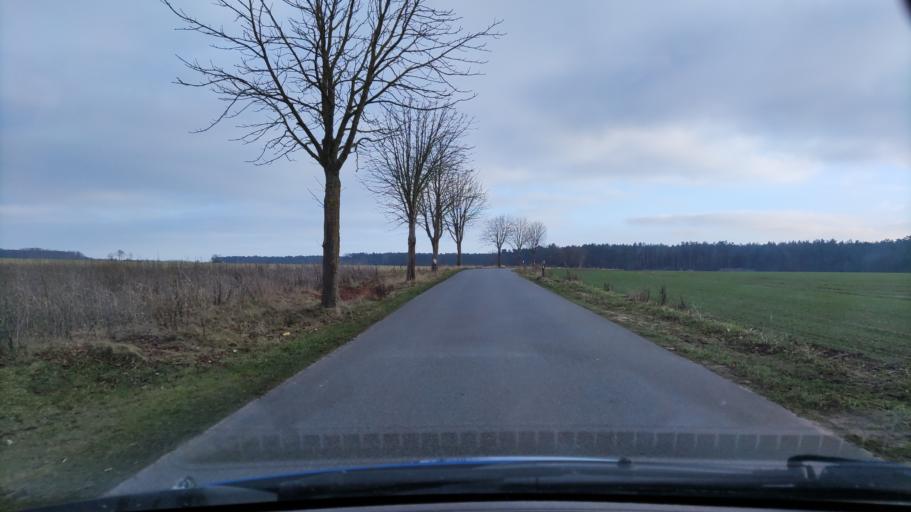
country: DE
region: Lower Saxony
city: Gerdau
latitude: 52.9542
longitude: 10.4262
